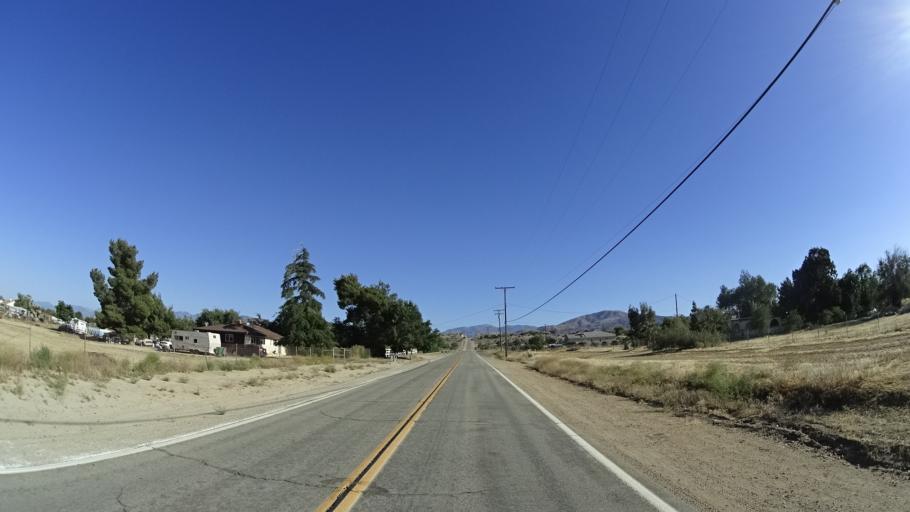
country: US
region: California
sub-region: Los Angeles County
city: Littlerock
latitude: 34.5376
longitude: -118.0277
